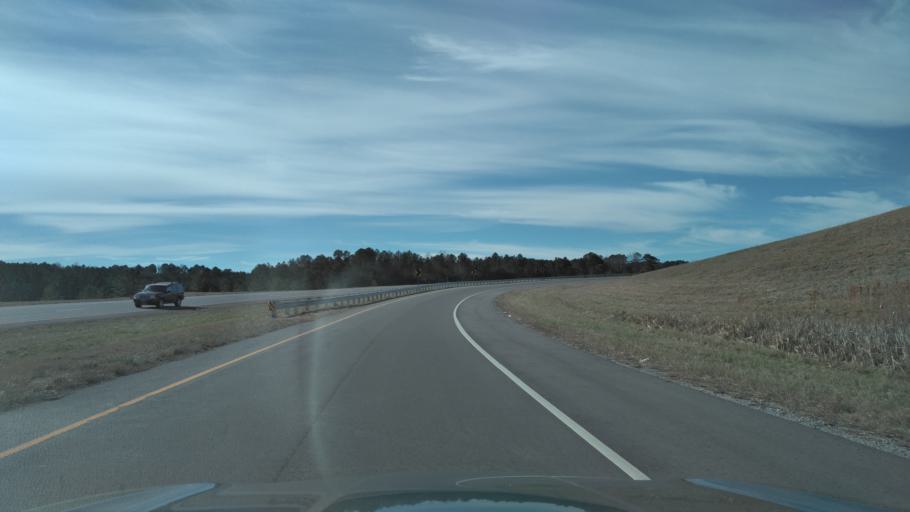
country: US
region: Alabama
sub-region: Walker County
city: Jasper
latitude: 33.8543
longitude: -87.3476
